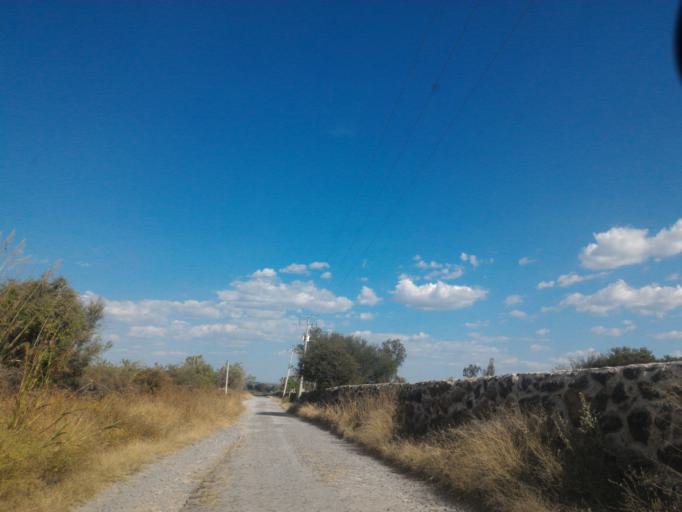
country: MX
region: Jalisco
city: San Diego de Alejandria
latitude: 20.8850
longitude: -101.9933
